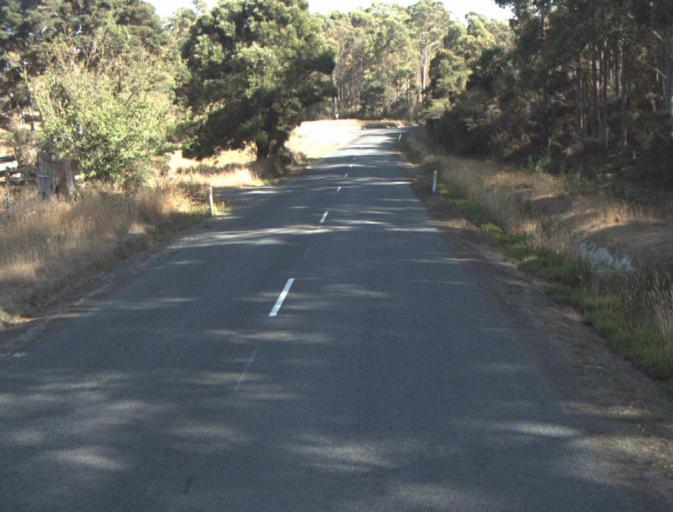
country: AU
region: Tasmania
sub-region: Dorset
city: Bridport
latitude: -41.1612
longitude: 147.2399
